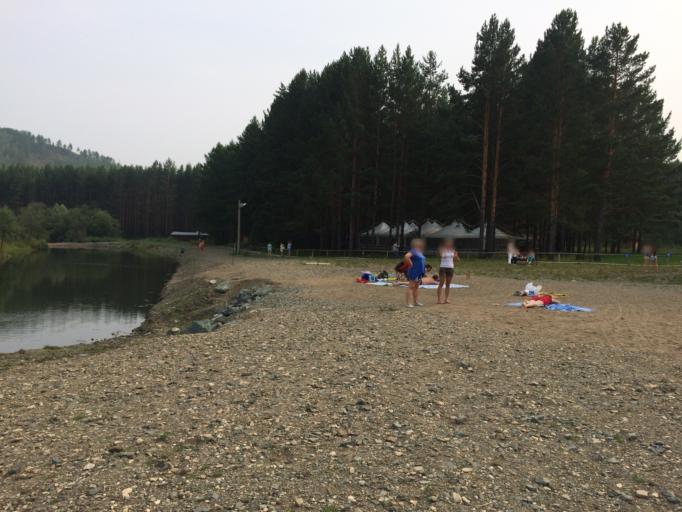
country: RU
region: Bashkortostan
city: Abzakovo
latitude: 53.7964
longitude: 58.6301
